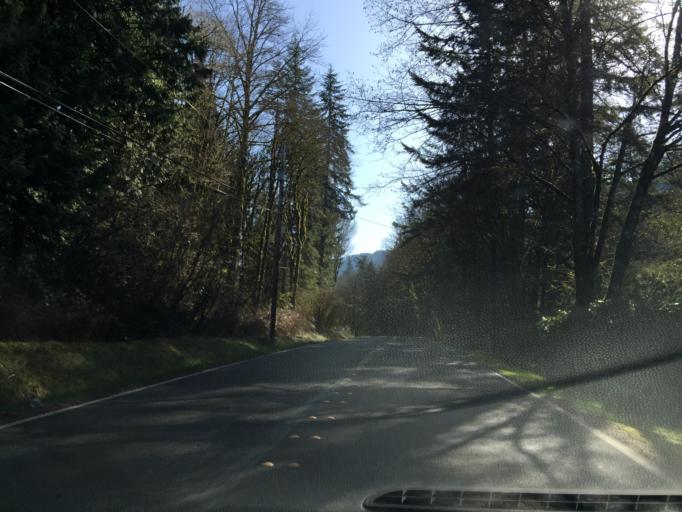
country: US
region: Washington
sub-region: Whatcom County
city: Bellingham
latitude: 48.6988
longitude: -122.4691
